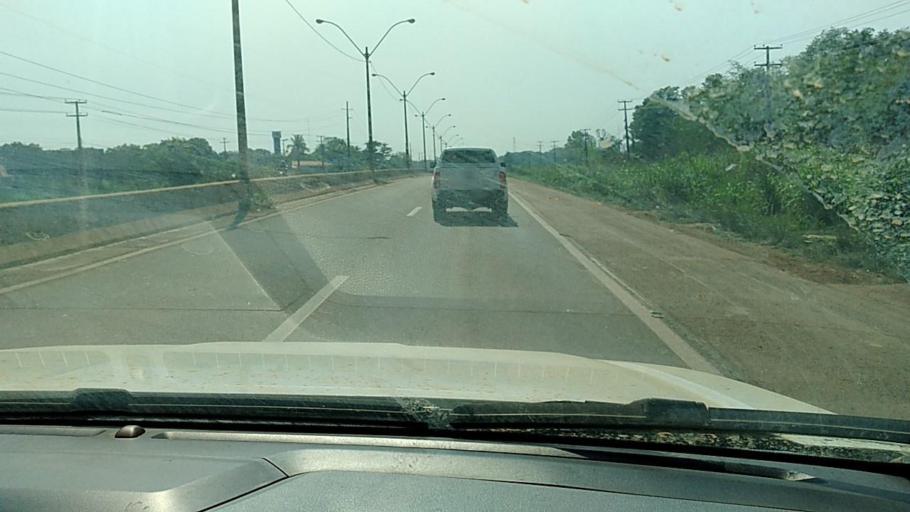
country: BR
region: Rondonia
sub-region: Porto Velho
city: Porto Velho
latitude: -8.8001
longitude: -63.8099
